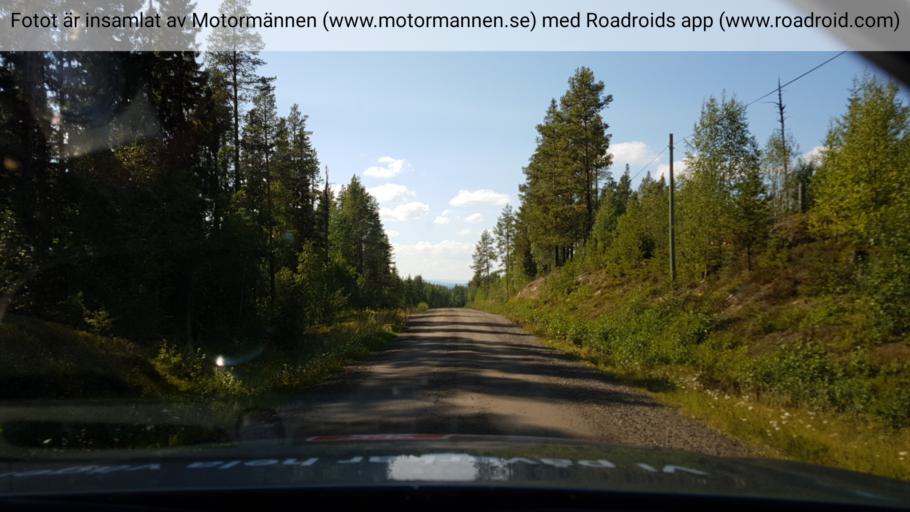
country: SE
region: Vaesterbotten
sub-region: Dorotea Kommun
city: Dorotea
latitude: 64.0937
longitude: 16.4632
